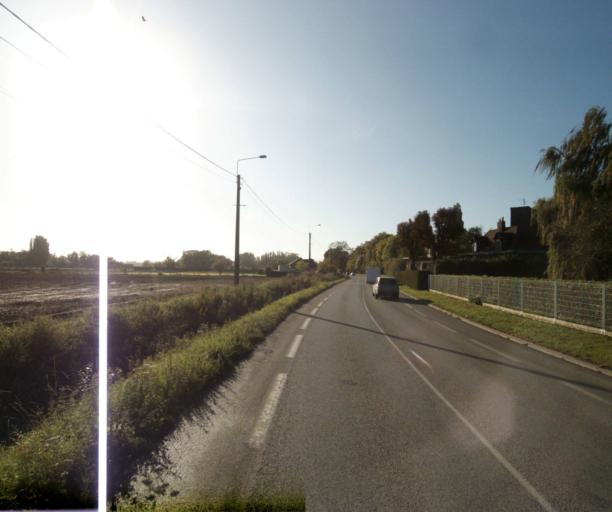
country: FR
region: Nord-Pas-de-Calais
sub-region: Departement du Nord
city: Verlinghem
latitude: 50.6747
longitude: 3.0017
